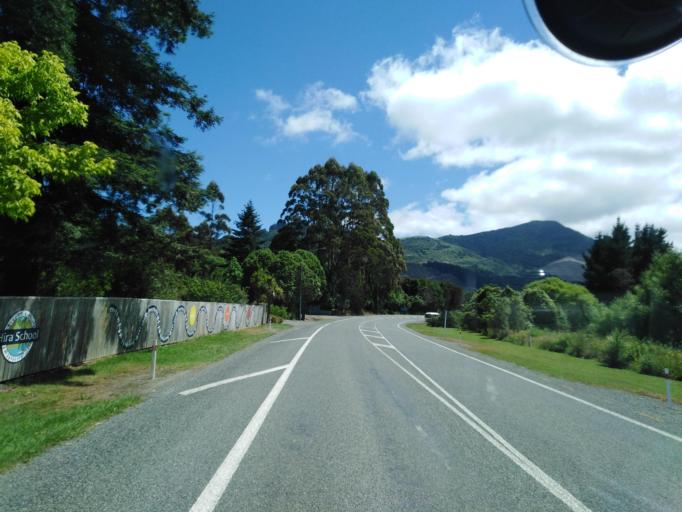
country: NZ
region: Nelson
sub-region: Nelson City
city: Nelson
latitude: -41.2167
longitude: 173.3955
